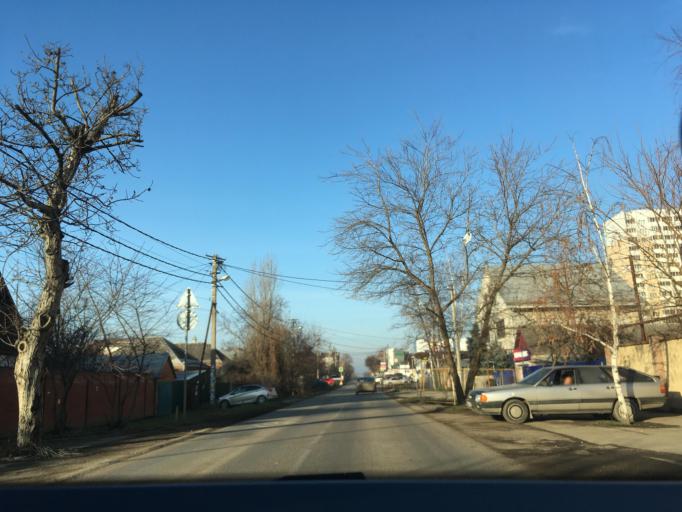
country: RU
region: Krasnodarskiy
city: Krasnodar
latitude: 45.0696
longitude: 39.0216
